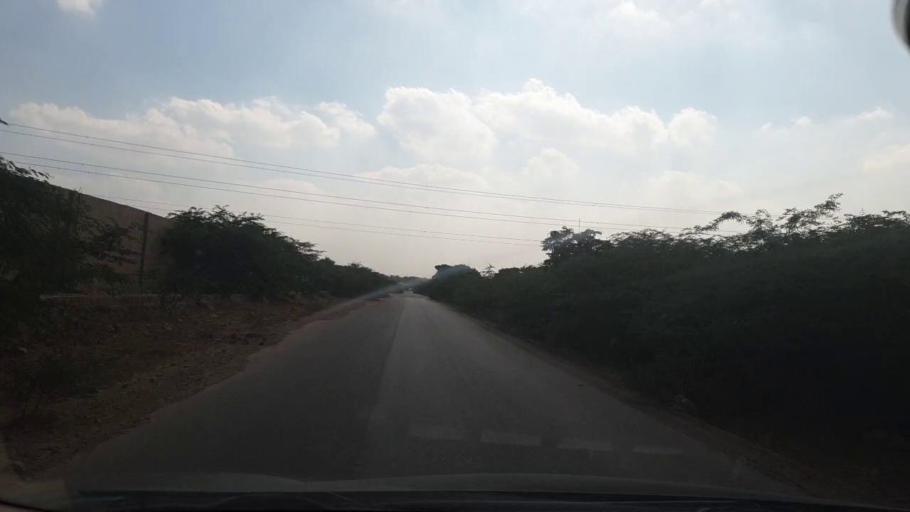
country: PK
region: Sindh
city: Malir Cantonment
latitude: 25.0109
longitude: 67.3544
